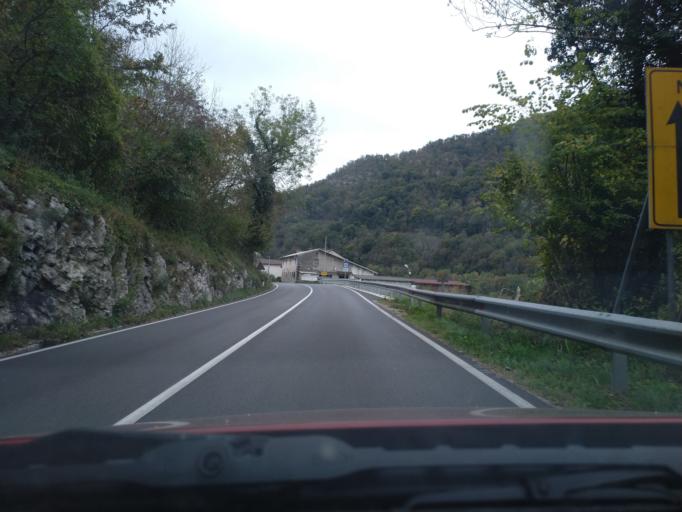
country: SI
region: Kanal
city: Deskle
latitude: 46.0415
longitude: 13.5903
